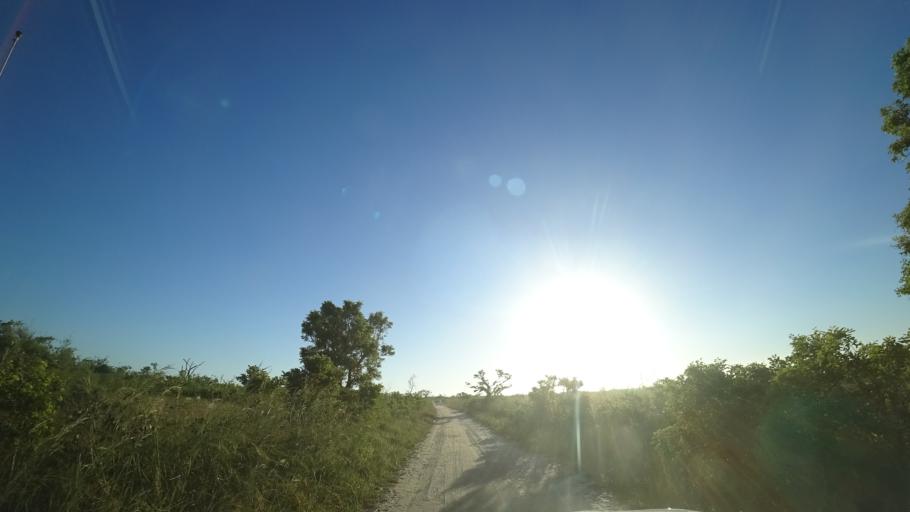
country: MZ
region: Sofala
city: Dondo
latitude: -19.5773
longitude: 35.1164
